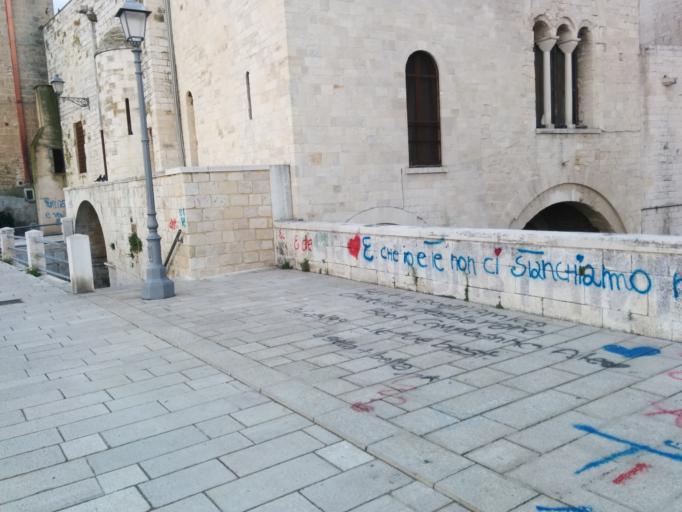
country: IT
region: Apulia
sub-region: Provincia di Bari
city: Bari
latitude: 41.1303
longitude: 16.8708
